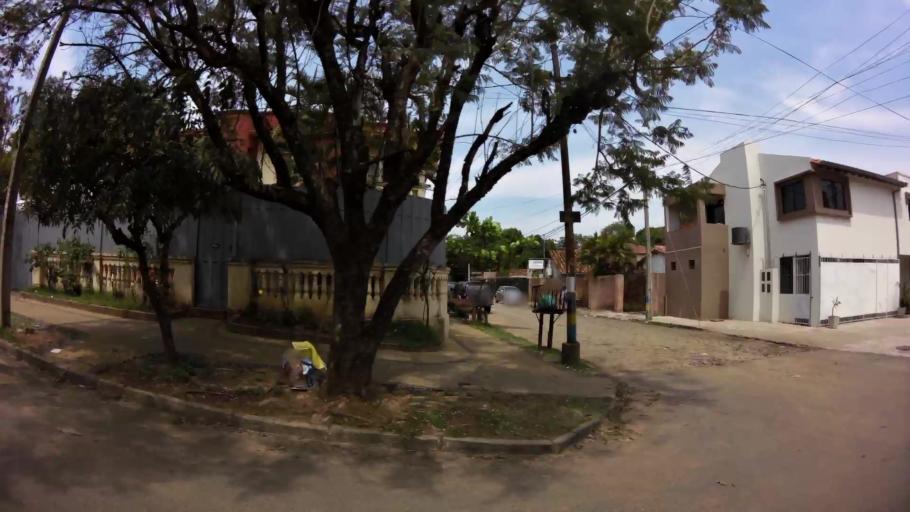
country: PY
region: Asuncion
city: Asuncion
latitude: -25.2596
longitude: -57.5823
